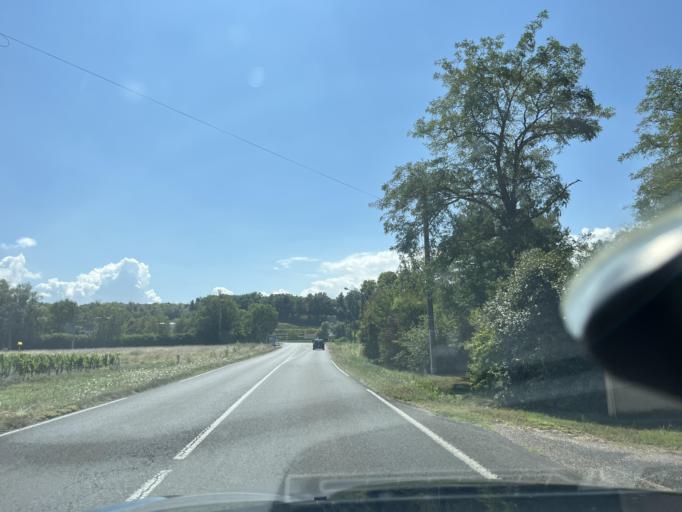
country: FR
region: Aquitaine
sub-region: Departement de la Gironde
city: Cars
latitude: 45.0814
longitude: -0.6366
